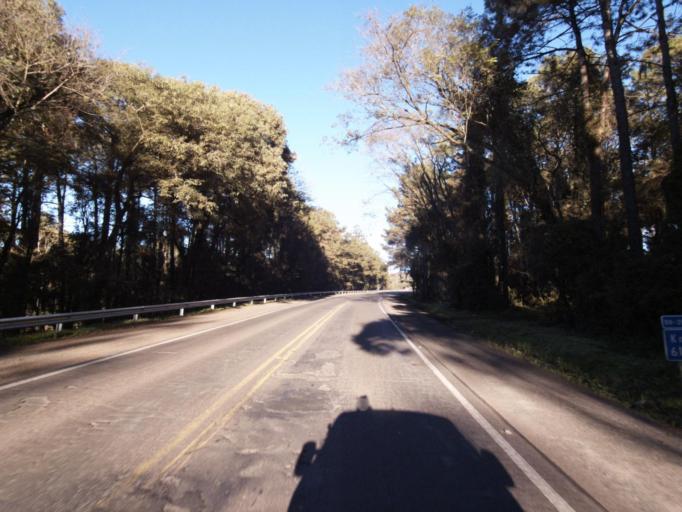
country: BR
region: Santa Catarina
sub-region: Sao Lourenco Do Oeste
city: Sao Lourenco dOeste
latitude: -26.7632
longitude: -53.2519
